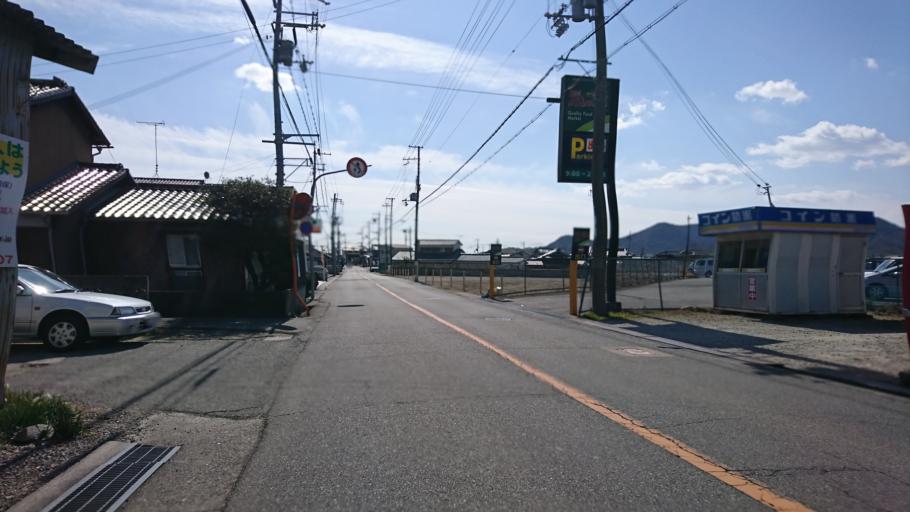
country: JP
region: Hyogo
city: Kakogawacho-honmachi
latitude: 34.8155
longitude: 134.8187
